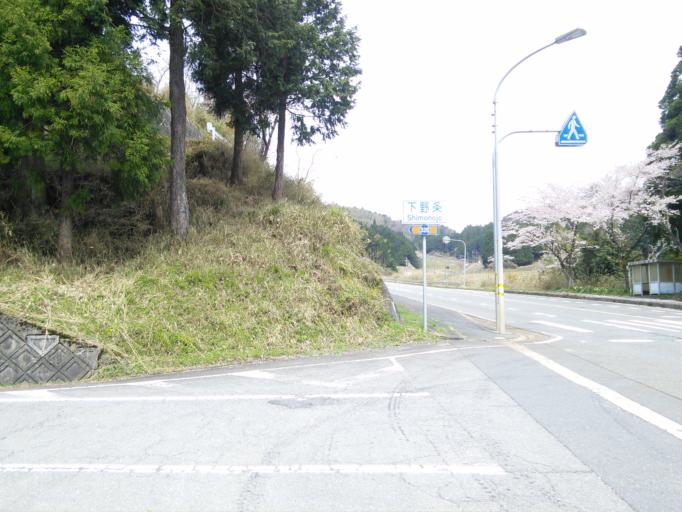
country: JP
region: Kyoto
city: Fukuchiyama
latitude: 35.4037
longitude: 135.0821
